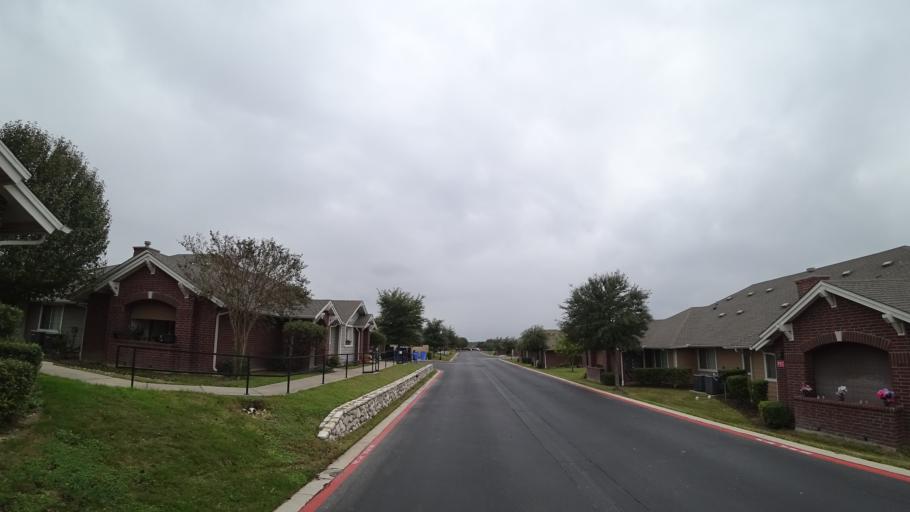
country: US
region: Texas
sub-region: Travis County
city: Pflugerville
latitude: 30.4310
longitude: -97.6196
